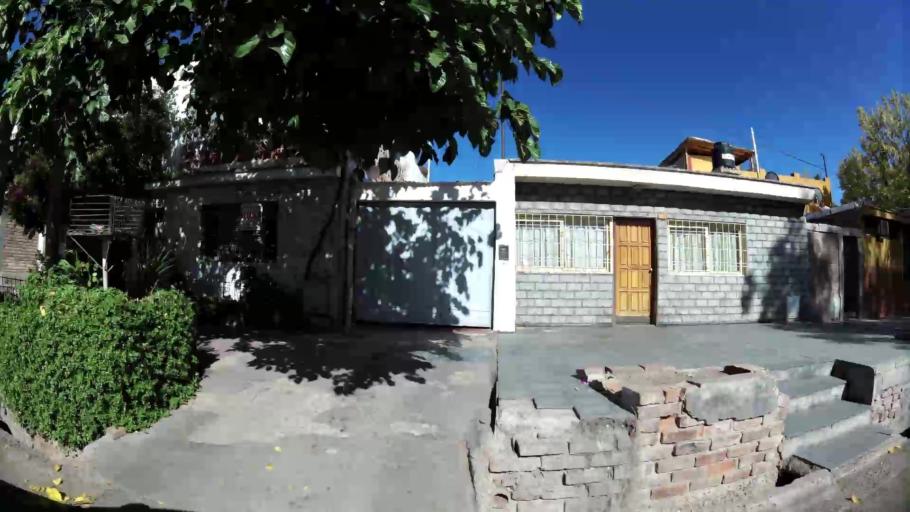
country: AR
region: Mendoza
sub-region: Departamento de Godoy Cruz
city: Godoy Cruz
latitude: -32.9291
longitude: -68.8626
